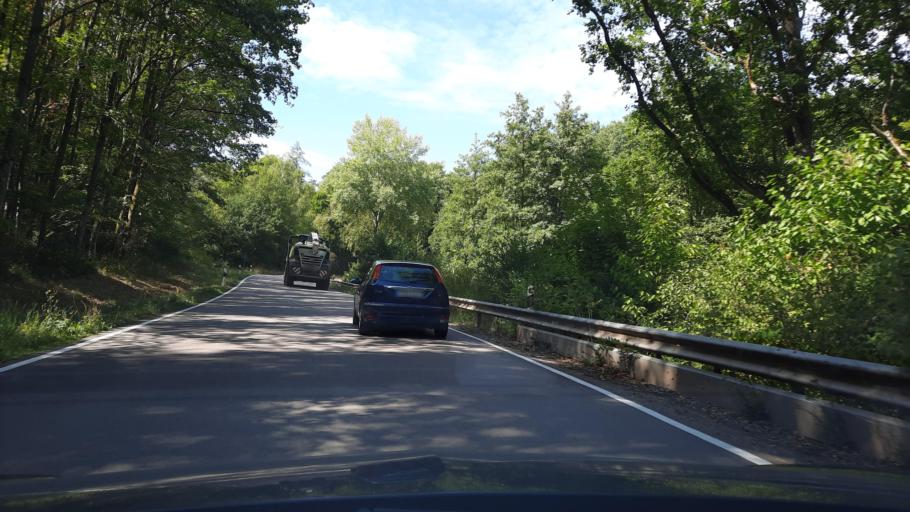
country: DE
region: Rheinland-Pfalz
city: Mannebach
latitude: 49.6275
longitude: 6.5317
